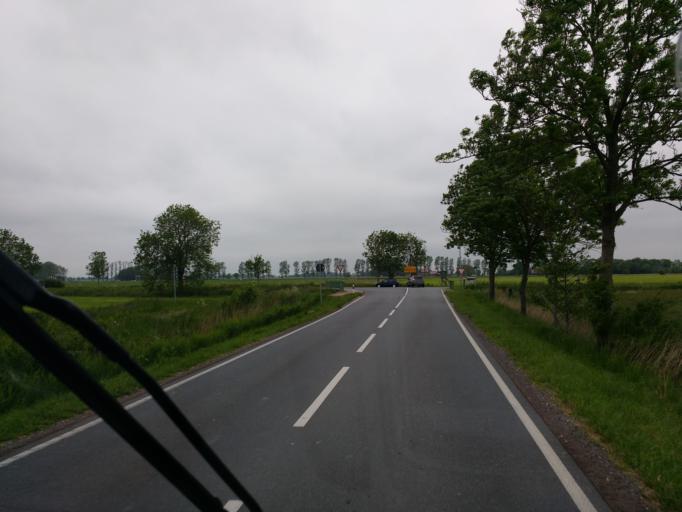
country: DE
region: Lower Saxony
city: Jever
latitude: 53.6115
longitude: 7.9338
